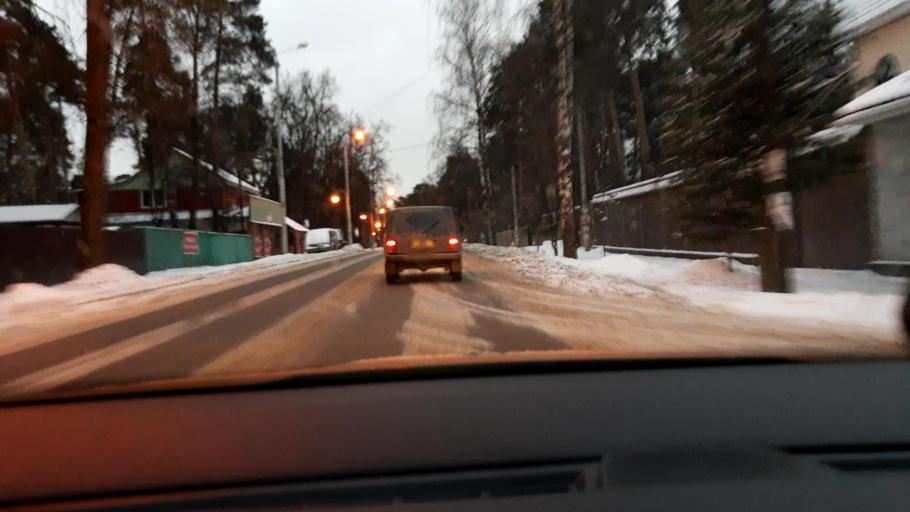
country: RU
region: Moskovskaya
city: Tomilino
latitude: 55.6515
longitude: 37.9540
